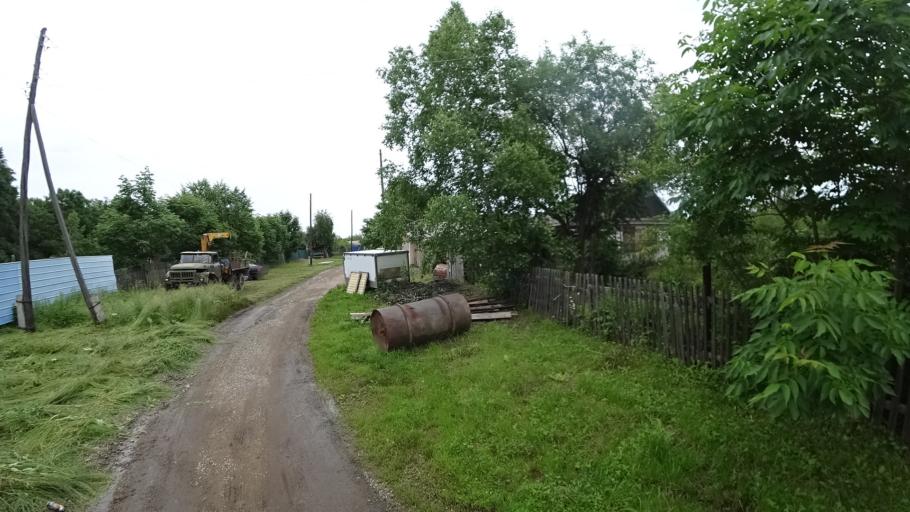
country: RU
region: Primorskiy
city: Novosysoyevka
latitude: 44.2069
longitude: 133.3406
